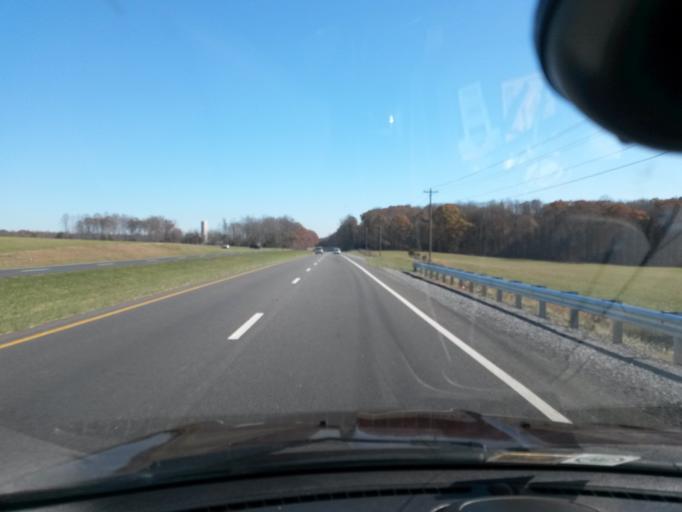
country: US
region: Virginia
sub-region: Bedford County
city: Forest
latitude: 37.3007
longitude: -79.3462
